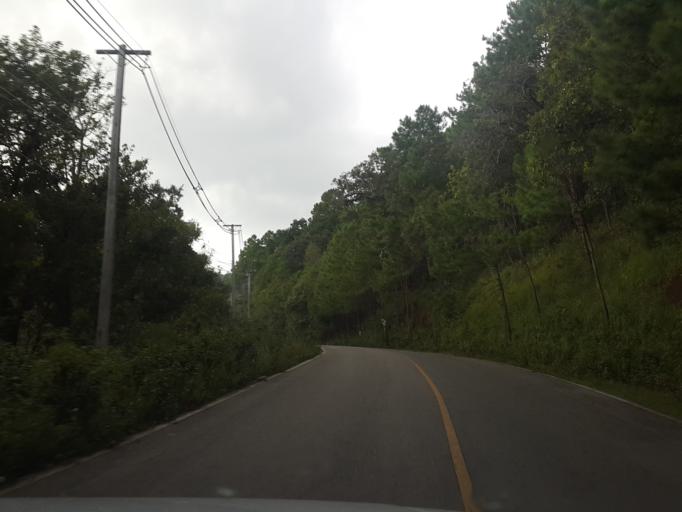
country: TH
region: Mae Hong Son
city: Khun Yuam
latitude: 18.7647
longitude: 98.1740
